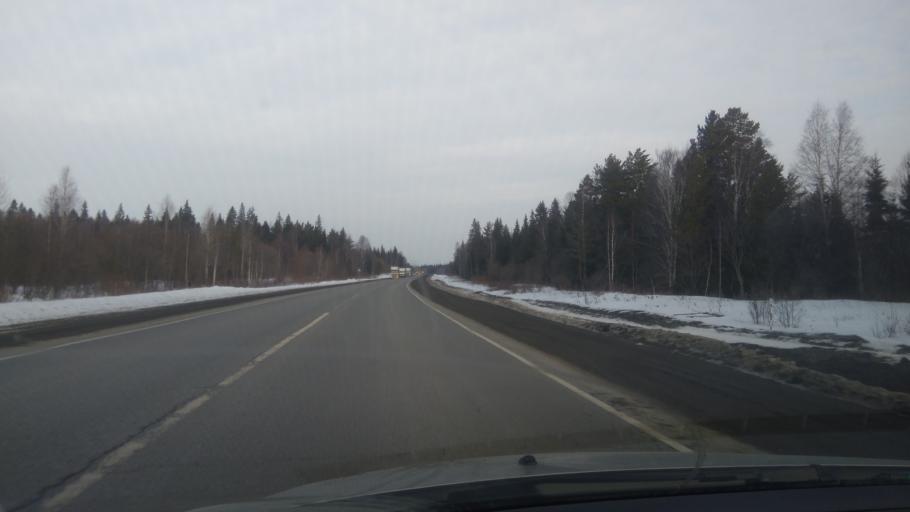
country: RU
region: Sverdlovsk
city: Atig
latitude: 56.8043
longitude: 59.3751
